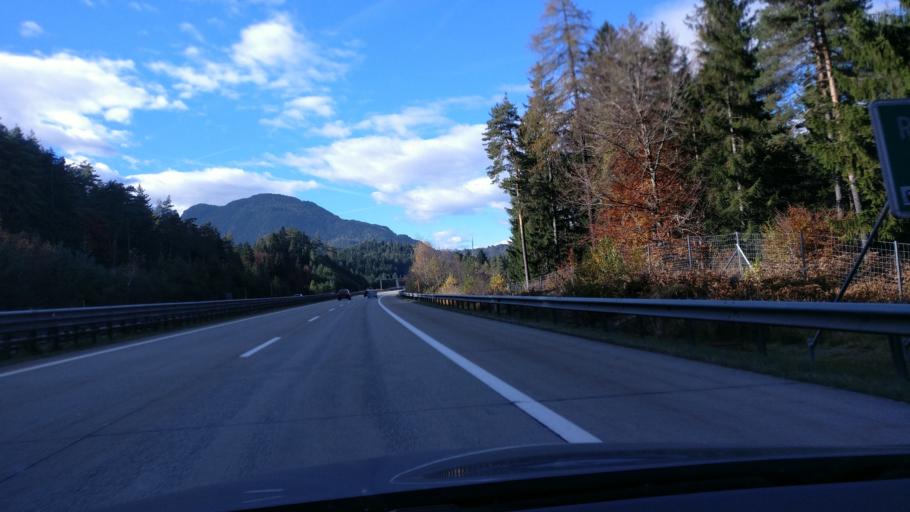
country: AT
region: Carinthia
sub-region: Politischer Bezirk Villach Land
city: Fresach
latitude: 46.6513
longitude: 13.7471
